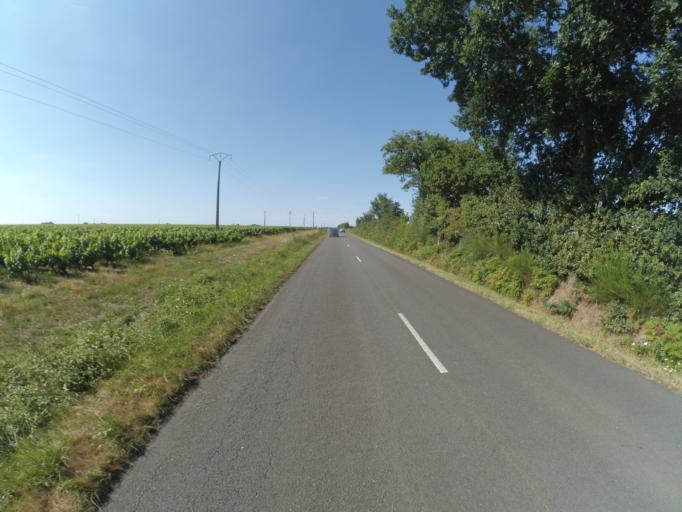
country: FR
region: Pays de la Loire
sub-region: Departement de la Loire-Atlantique
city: Maisdon-sur-Sevre
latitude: 47.0846
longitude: -1.3884
